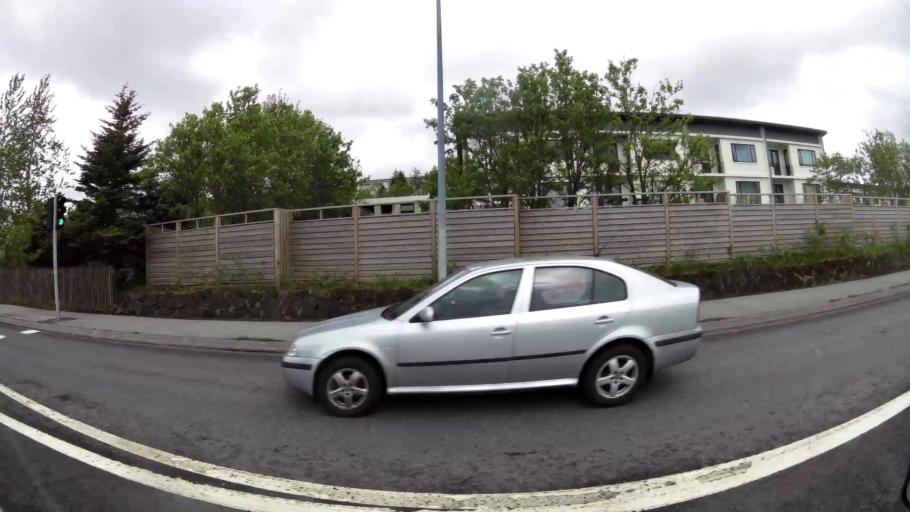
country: IS
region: Capital Region
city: Reykjavik
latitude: 64.1212
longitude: -21.8644
